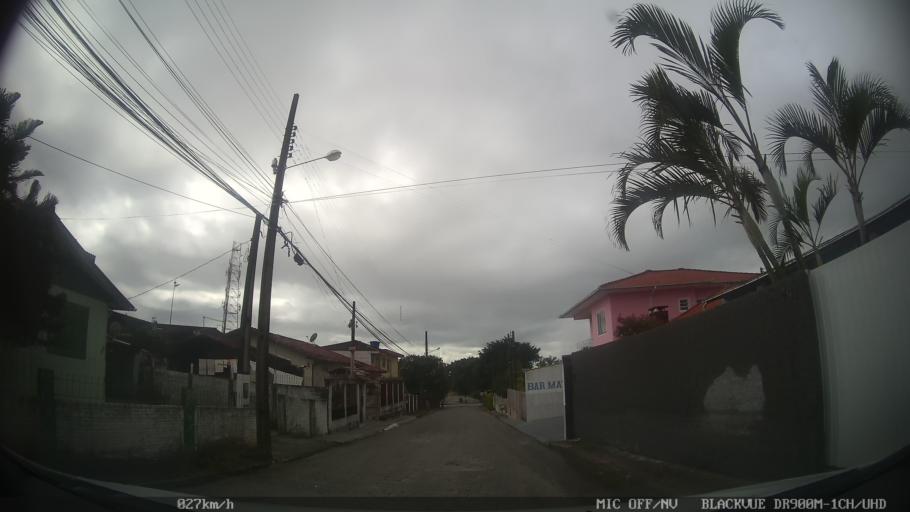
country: BR
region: Santa Catarina
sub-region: Biguacu
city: Biguacu
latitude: -27.5323
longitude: -48.6351
